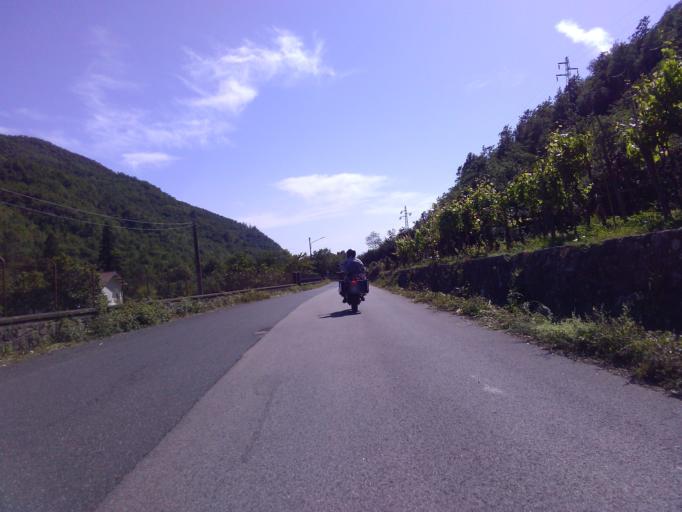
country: IT
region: Tuscany
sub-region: Provincia di Massa-Carrara
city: Licciana Nardi
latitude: 44.2814
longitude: 10.0641
